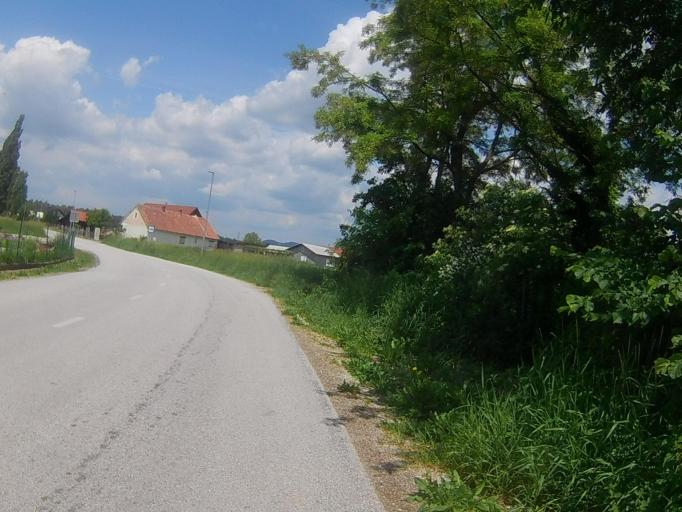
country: SI
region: Kidricevo
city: Kidricevo
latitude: 46.4273
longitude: 15.7819
